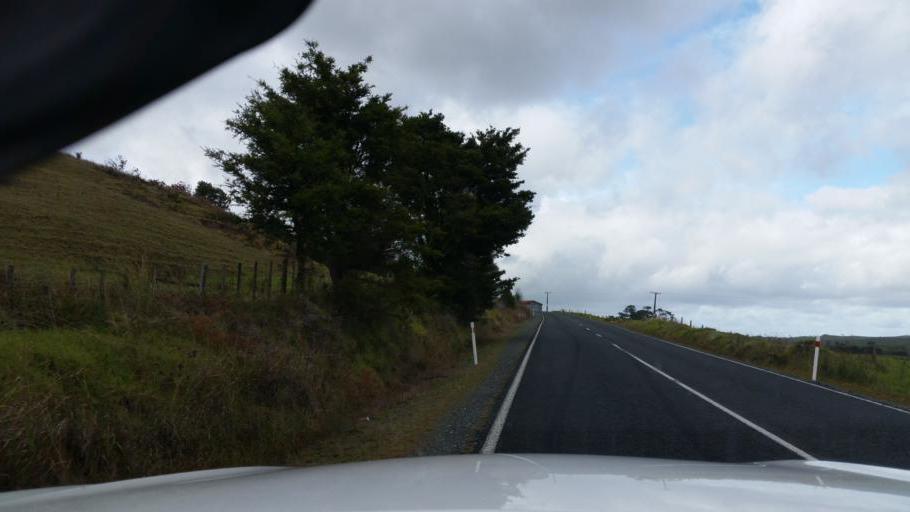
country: NZ
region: Northland
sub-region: Whangarei
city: Ruakaka
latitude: -35.9504
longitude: 174.2936
